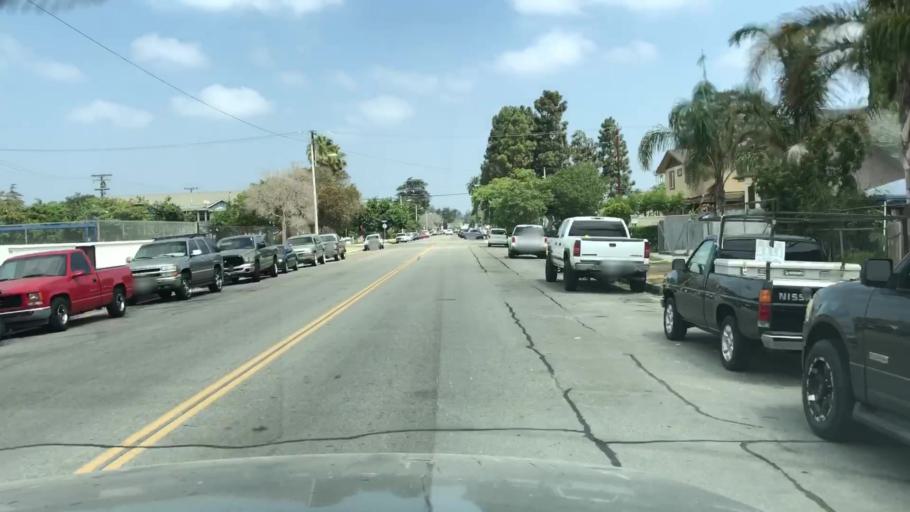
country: US
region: California
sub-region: Ventura County
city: Oxnard
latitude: 34.1993
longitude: -119.1823
